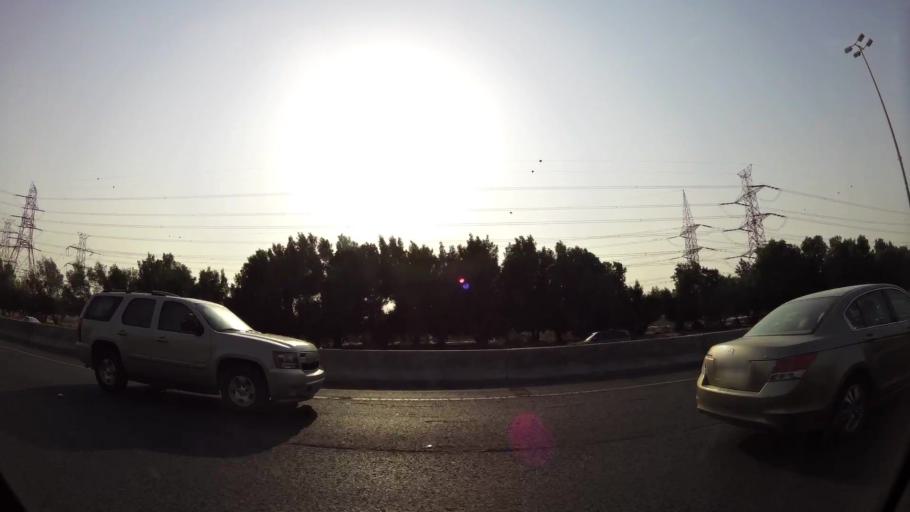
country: KW
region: Mubarak al Kabir
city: Sabah as Salim
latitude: 29.2729
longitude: 48.0387
